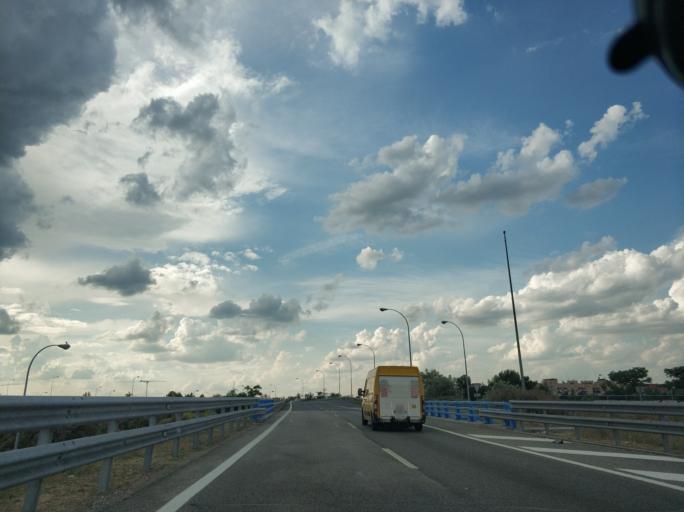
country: ES
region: Madrid
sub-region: Provincia de Madrid
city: Usera
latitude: 40.3801
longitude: -3.6864
